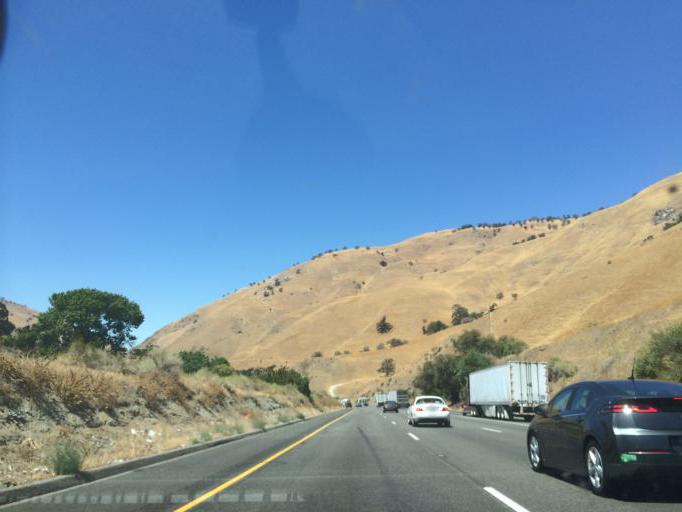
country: US
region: California
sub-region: Kern County
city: Lebec
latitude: 34.8813
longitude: -118.8991
